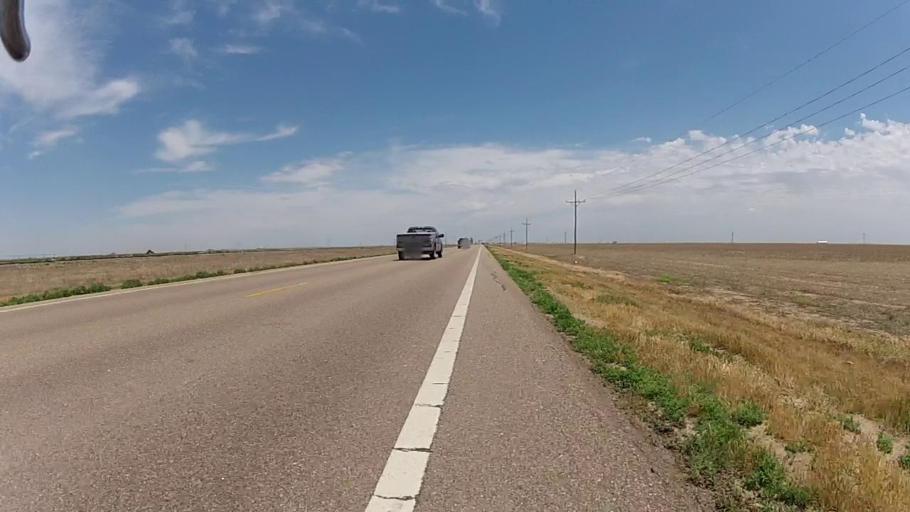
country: US
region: Kansas
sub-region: Haskell County
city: Sublette
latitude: 37.4665
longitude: -100.9044
